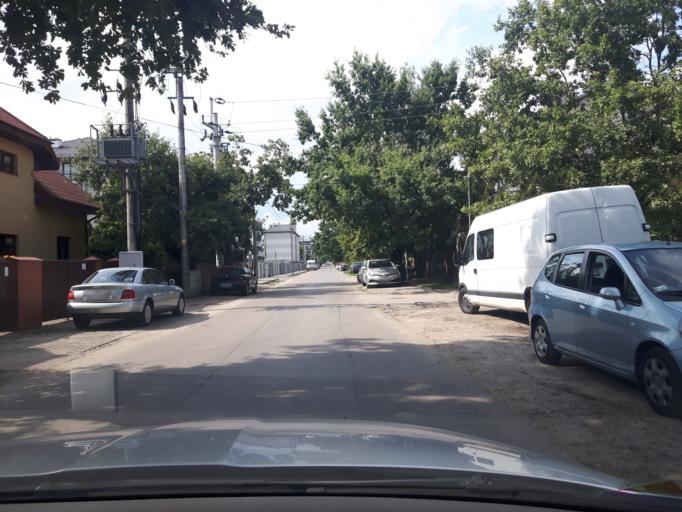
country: PL
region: Masovian Voivodeship
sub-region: Powiat wolominski
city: Marki
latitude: 52.3082
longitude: 21.1027
